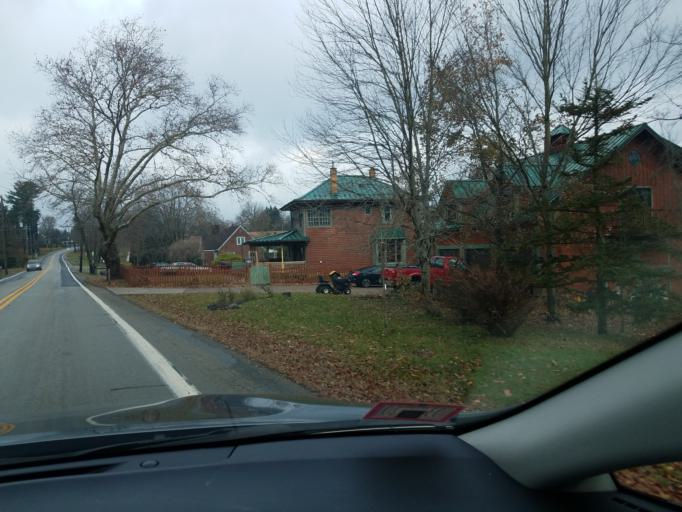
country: US
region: Pennsylvania
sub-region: Allegheny County
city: Franklin Park
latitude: 40.5752
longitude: -80.0756
